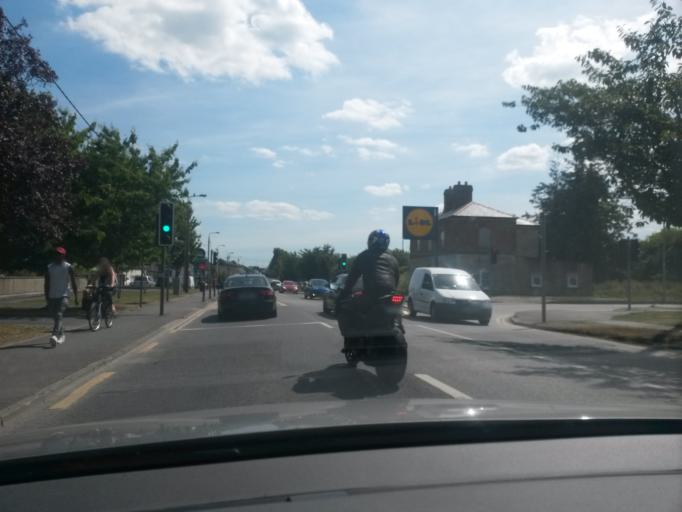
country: IE
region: Leinster
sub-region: Kildare
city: Sallins
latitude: 53.2512
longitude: -6.6652
